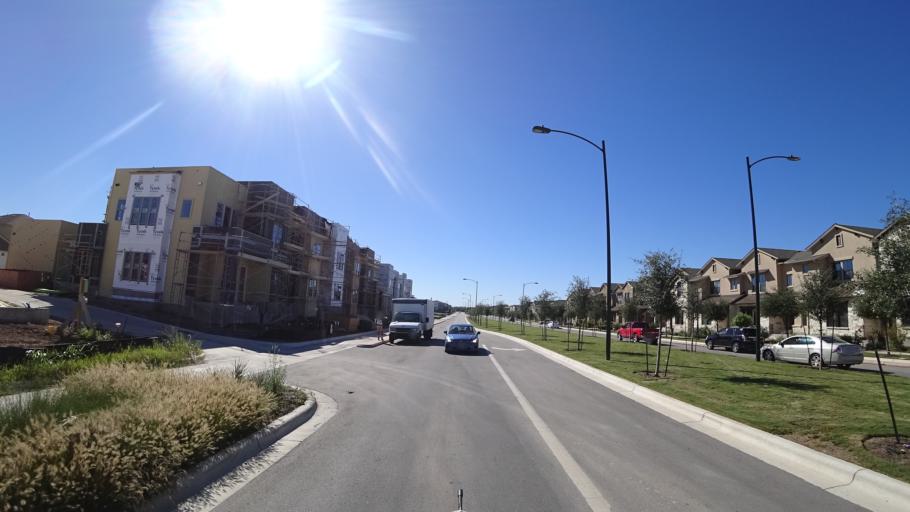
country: US
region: Texas
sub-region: Travis County
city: Austin
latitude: 30.2984
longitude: -97.7002
